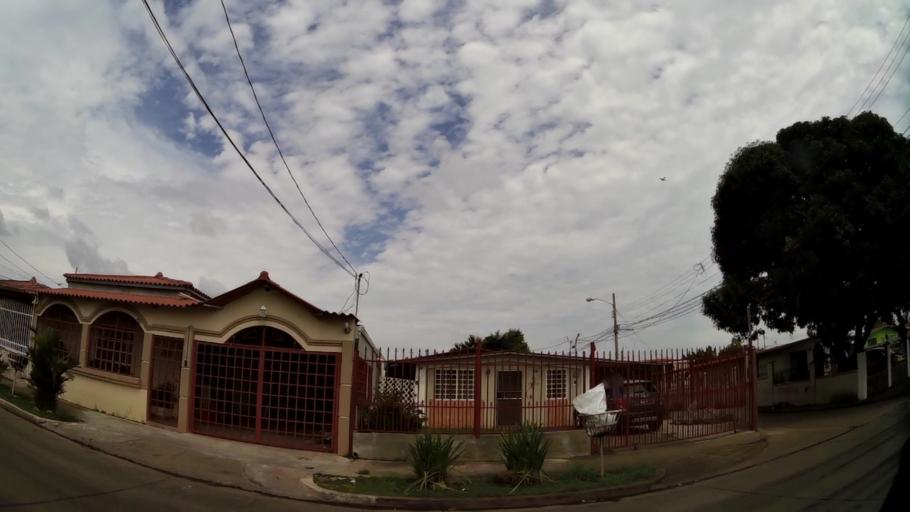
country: PA
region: Panama
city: Tocumen
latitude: 9.0483
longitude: -79.4130
